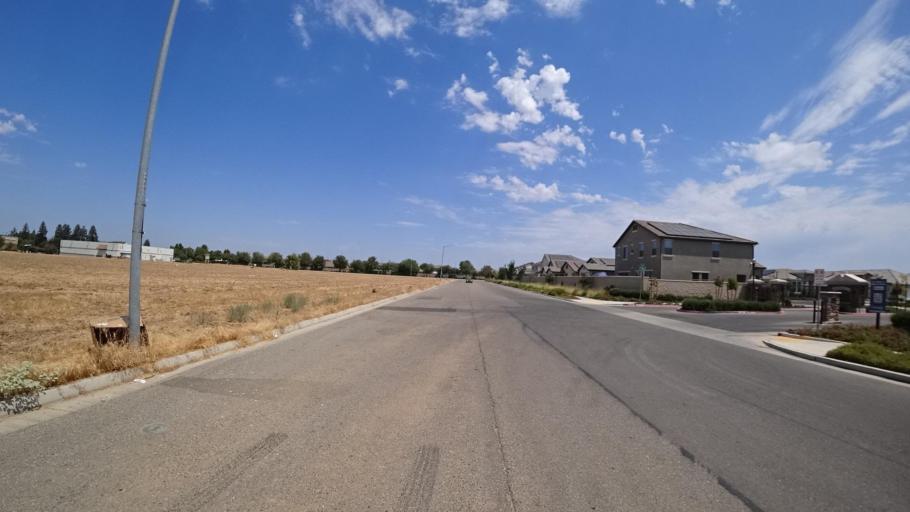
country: US
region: California
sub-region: Fresno County
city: Tarpey Village
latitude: 36.7776
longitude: -119.6795
